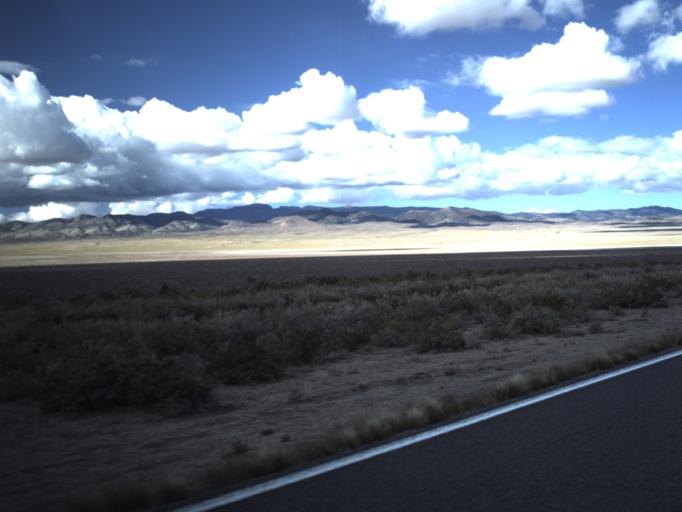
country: US
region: Utah
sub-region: Beaver County
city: Milford
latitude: 38.5474
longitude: -113.7225
